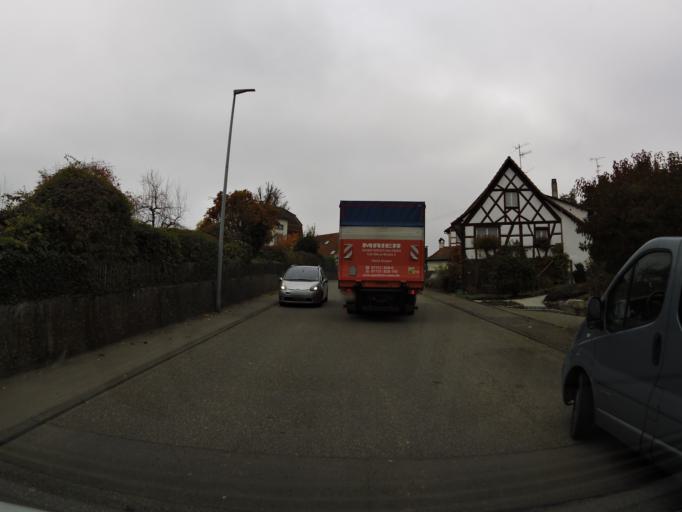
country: DE
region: Baden-Wuerttemberg
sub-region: Freiburg Region
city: Ohningen
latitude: 47.6608
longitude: 8.8921
